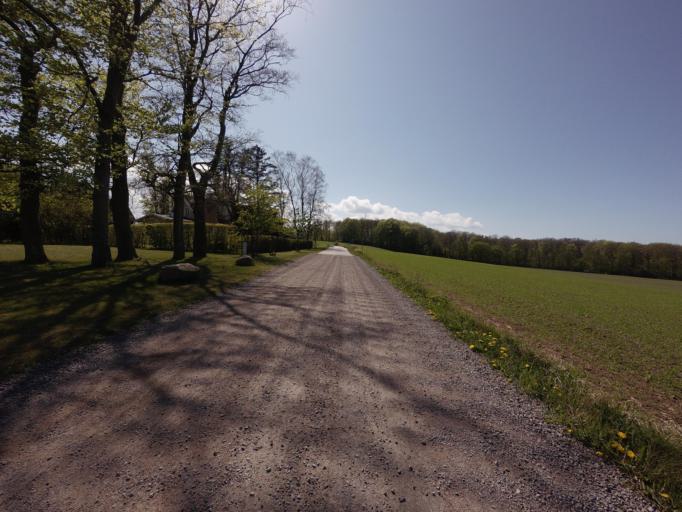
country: DK
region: Capital Region
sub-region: Helsingor Kommune
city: Hellebaek
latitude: 56.1255
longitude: 12.6220
